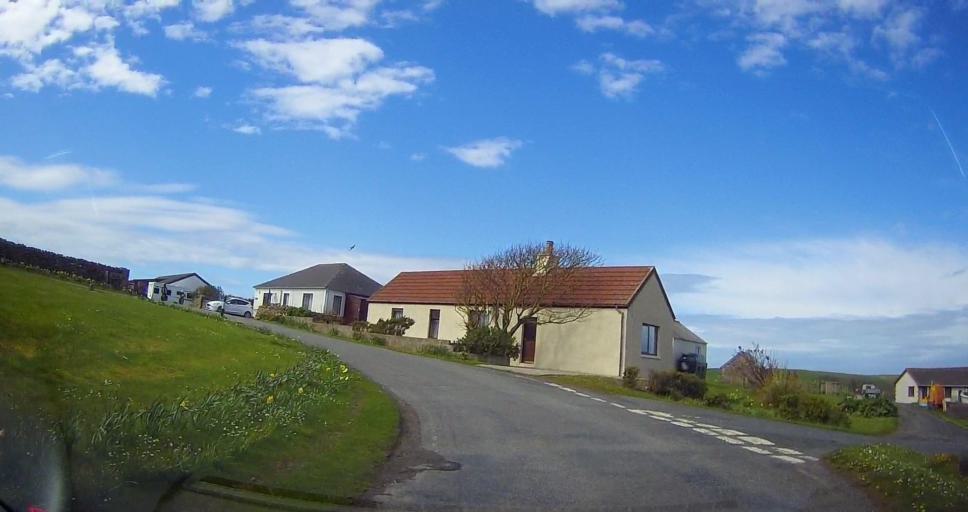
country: GB
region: Scotland
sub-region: Shetland Islands
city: Sandwick
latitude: 59.9734
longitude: -1.3243
